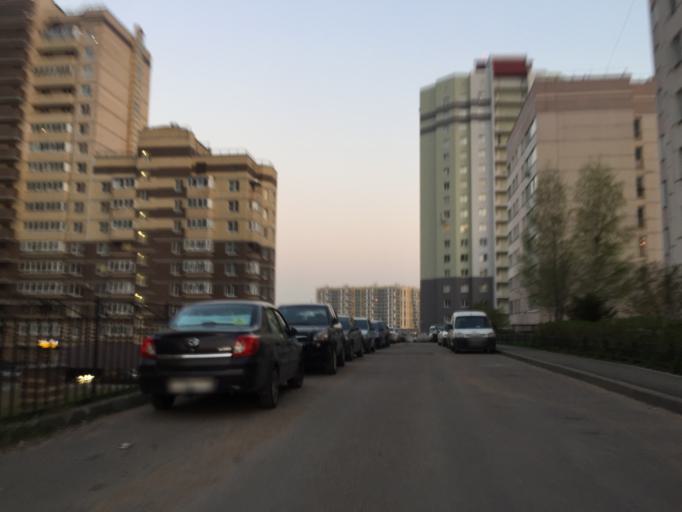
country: RU
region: Leningrad
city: Bugry
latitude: 60.0678
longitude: 30.4043
